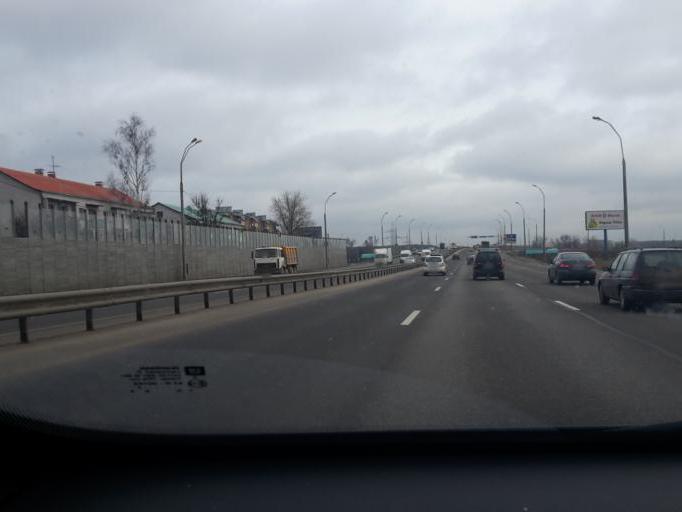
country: BY
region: Minsk
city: Zhdanovichy
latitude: 53.9387
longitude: 27.4299
